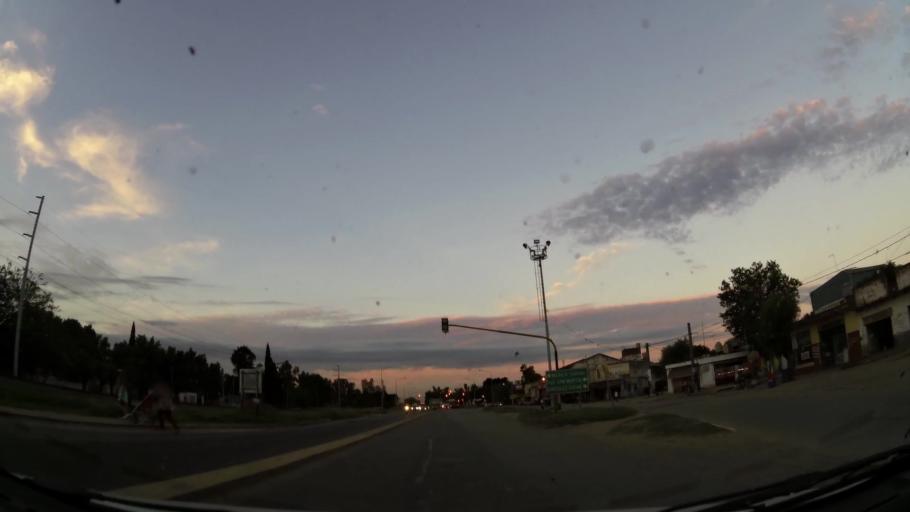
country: AR
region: Buenos Aires
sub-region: Partido de Merlo
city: Merlo
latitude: -34.6892
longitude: -58.7666
